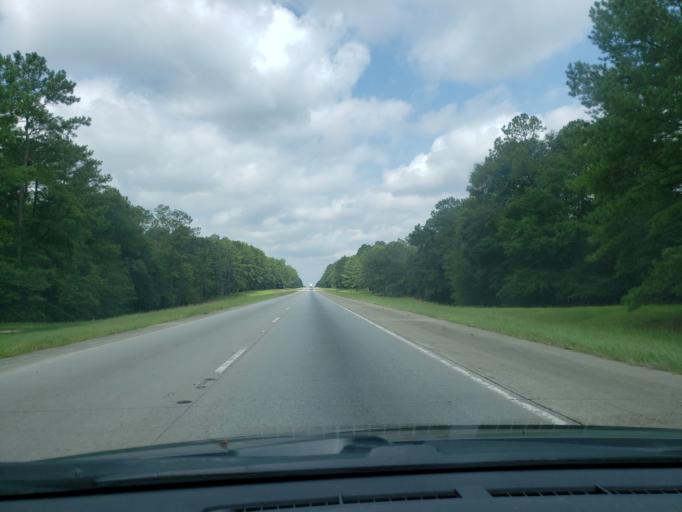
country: US
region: Georgia
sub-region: Emanuel County
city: Swainsboro
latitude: 32.4100
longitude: -82.3562
